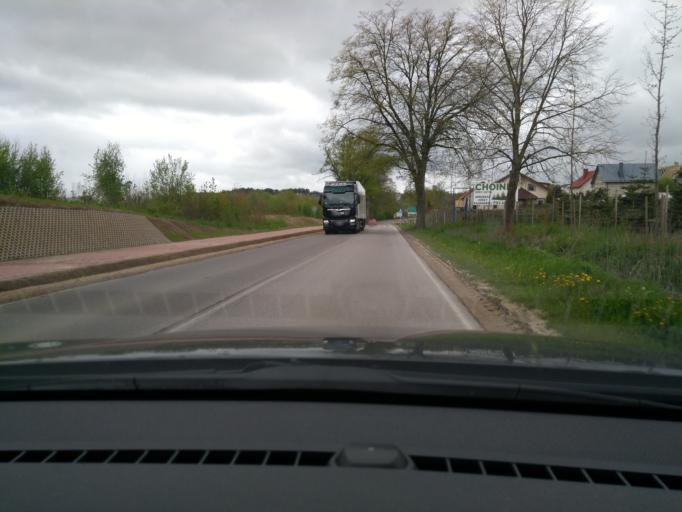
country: PL
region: Pomeranian Voivodeship
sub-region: Powiat kartuski
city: Sierakowice
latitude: 54.3406
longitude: 17.9141
